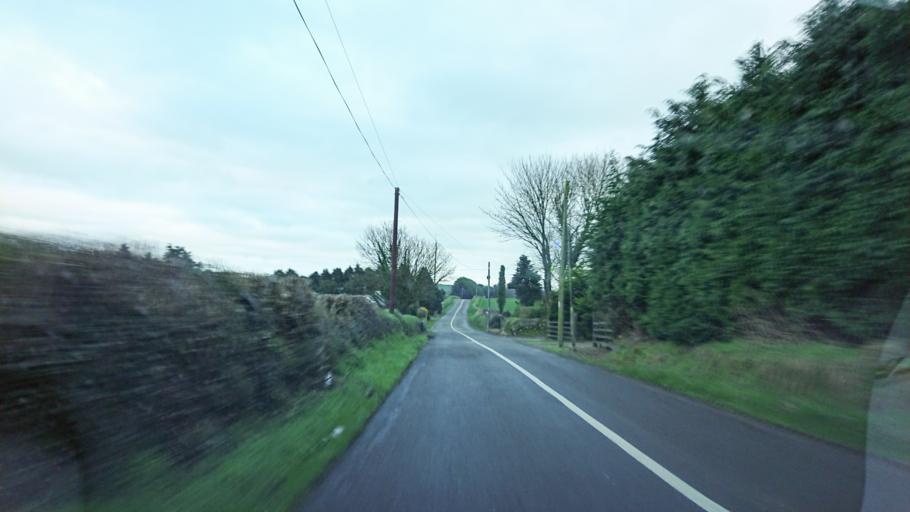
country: IE
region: Munster
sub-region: Waterford
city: Portlaw
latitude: 52.1952
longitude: -7.4223
